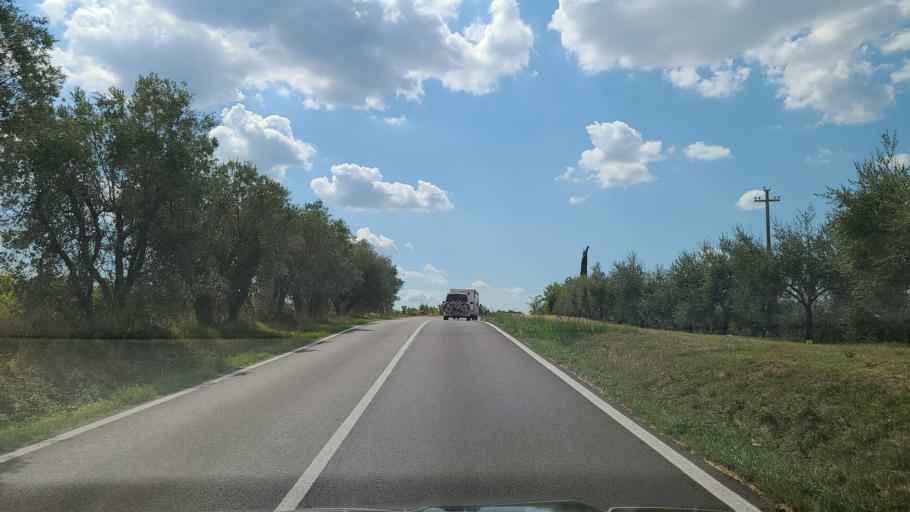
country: IT
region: Tuscany
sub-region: Provincia di Siena
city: Casole d'Elsa
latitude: 43.4070
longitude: 11.0512
